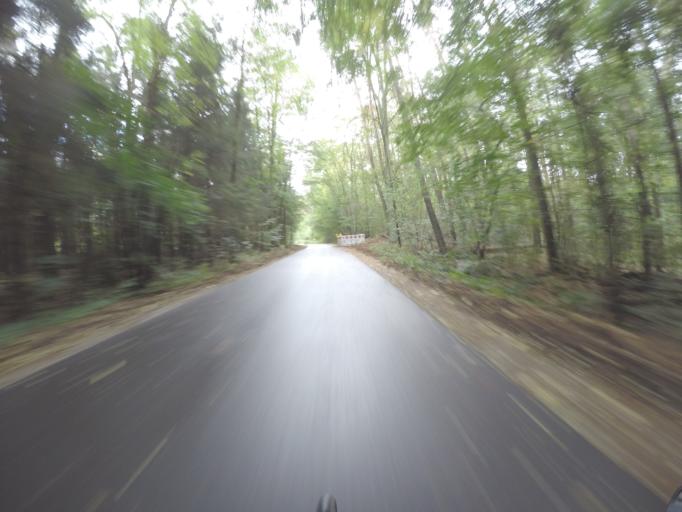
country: DE
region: Brandenburg
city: Strausberg
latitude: 52.6055
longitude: 13.9048
